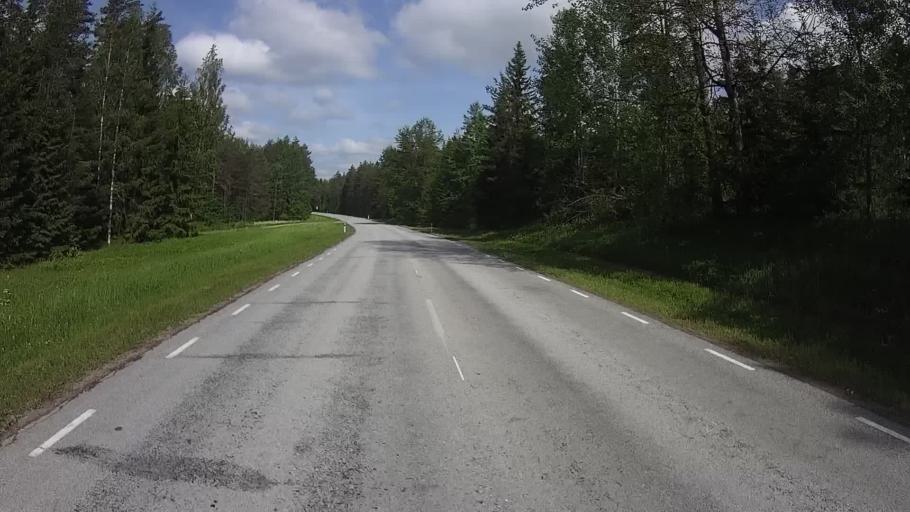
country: EE
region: Vorumaa
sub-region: Voru linn
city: Voru
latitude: 57.8700
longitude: 26.8162
